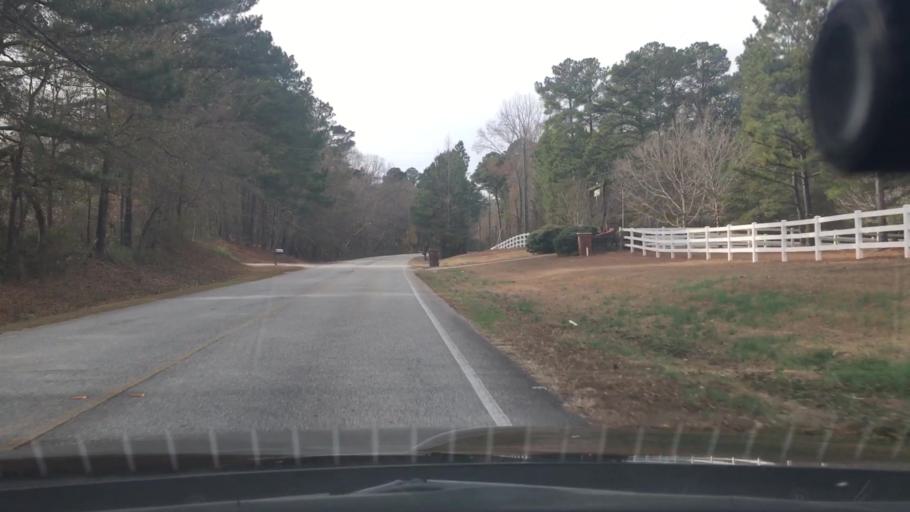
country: US
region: Georgia
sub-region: Coweta County
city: Senoia
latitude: 33.2880
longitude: -84.4495
